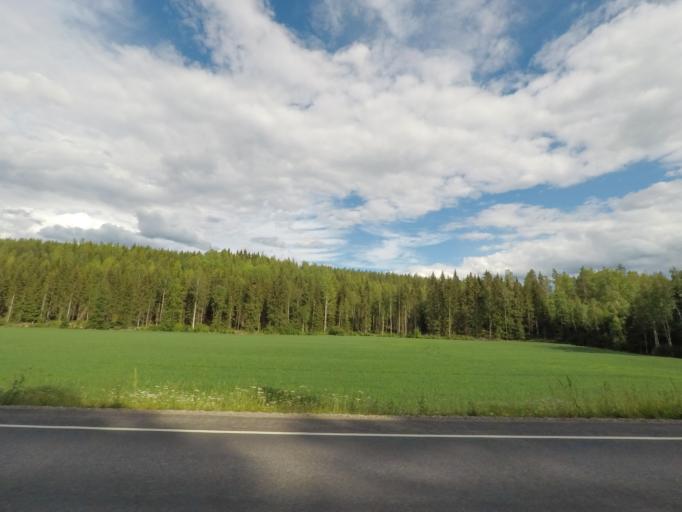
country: FI
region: Uusimaa
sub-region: Porvoo
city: Pukkila
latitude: 60.7861
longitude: 25.4615
